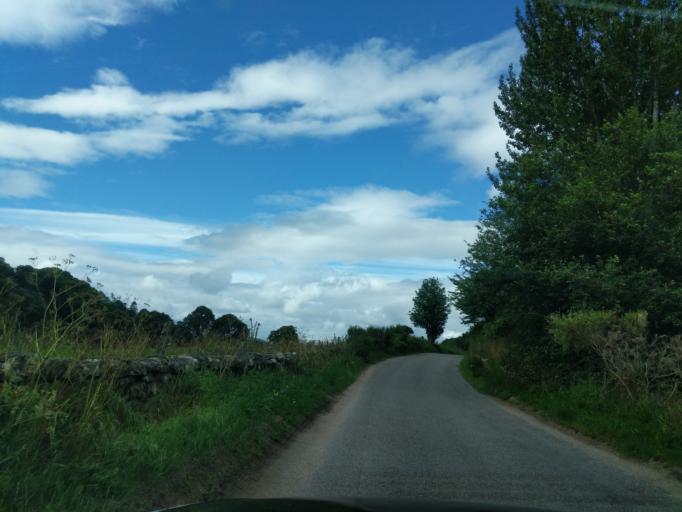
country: GB
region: Scotland
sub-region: Aberdeenshire
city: Ballater
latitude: 57.0441
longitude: -3.1617
